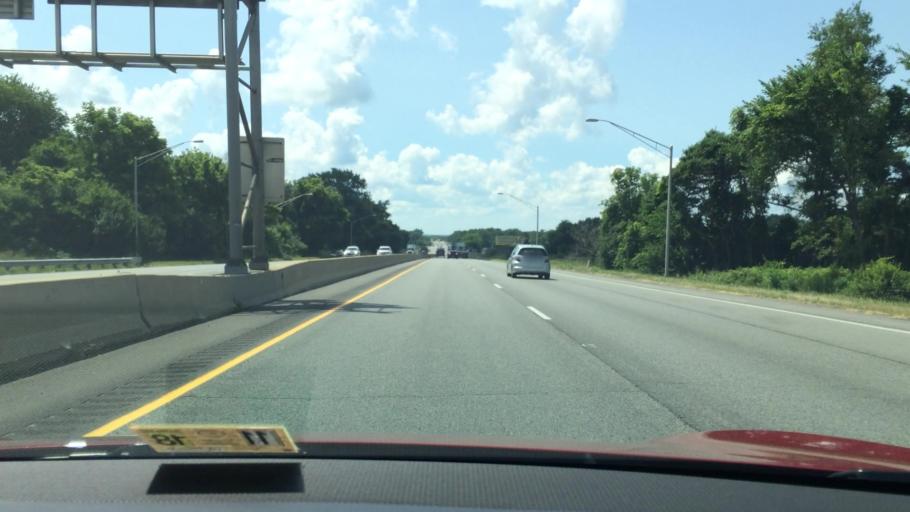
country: US
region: Indiana
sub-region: Saint Joseph County
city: South Bend
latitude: 41.7014
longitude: -86.3402
